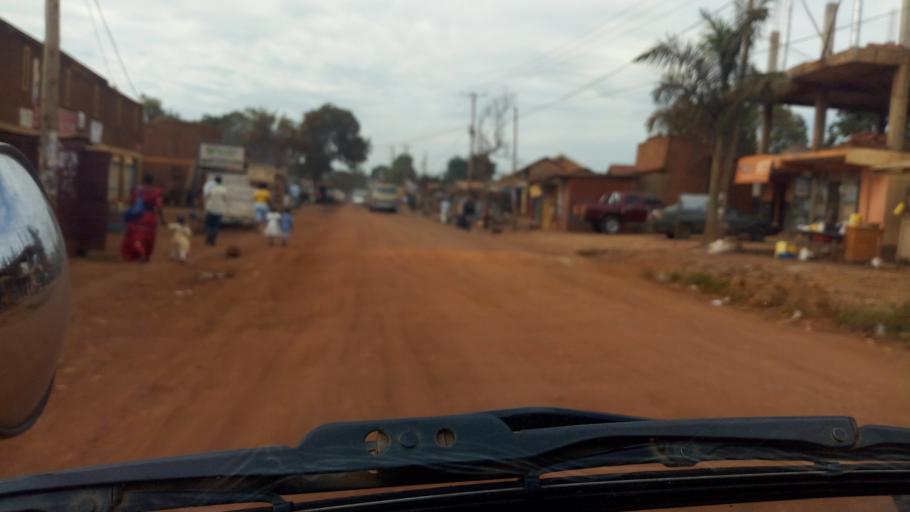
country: UG
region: Central Region
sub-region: Wakiso District
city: Bweyogerere
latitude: 0.3608
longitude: 32.7033
